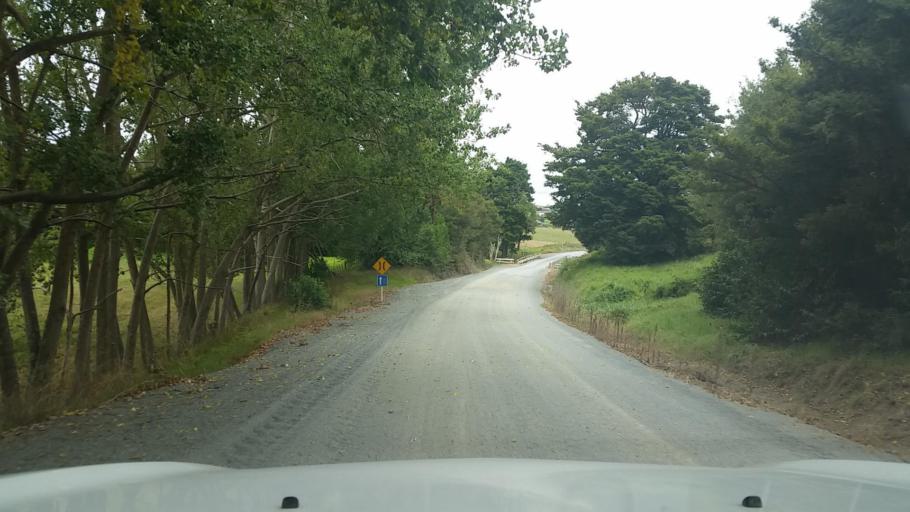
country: NZ
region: Northland
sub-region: Whangarei
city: Maungatapere
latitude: -35.6965
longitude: 174.1447
